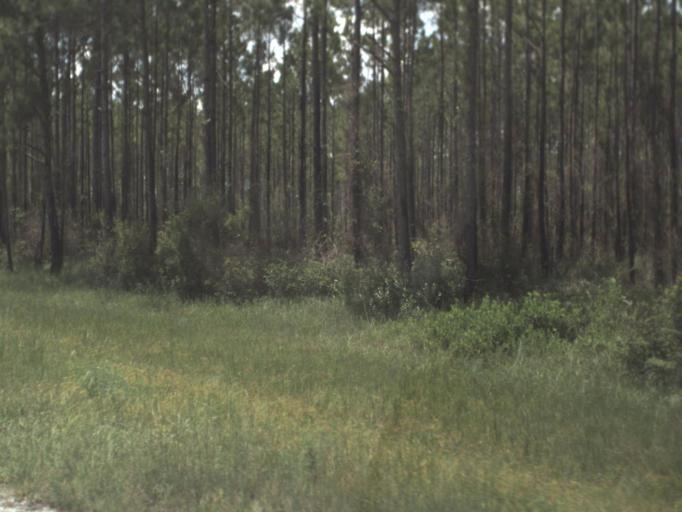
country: US
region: Florida
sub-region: Baker County
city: Macclenny
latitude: 30.5477
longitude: -82.3531
